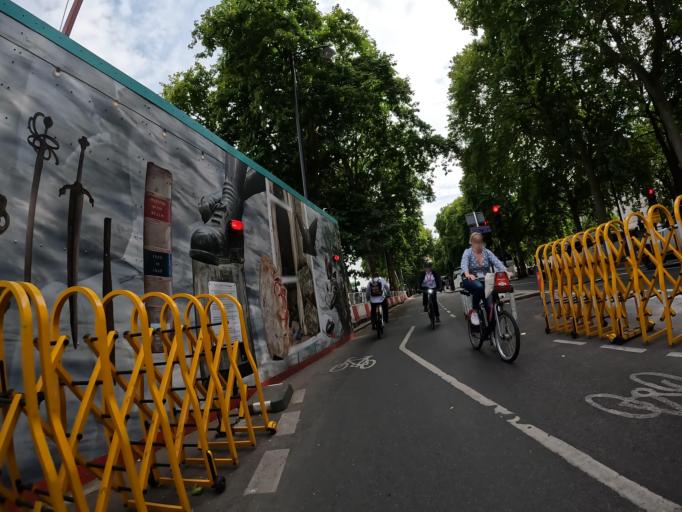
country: GB
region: England
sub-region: Greater London
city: Blackheath
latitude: 51.4420
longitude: 0.0046
